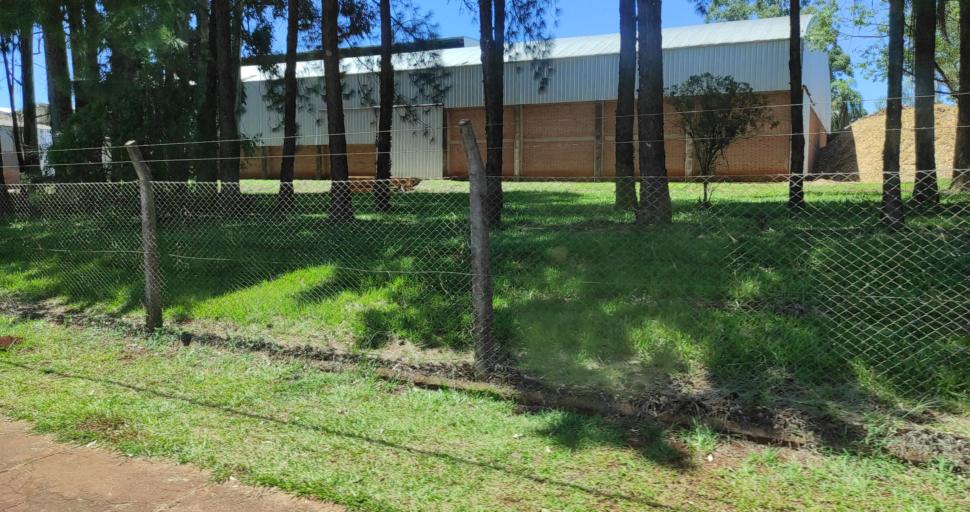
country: AR
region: Misiones
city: Dos de Mayo
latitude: -27.0064
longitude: -54.4791
